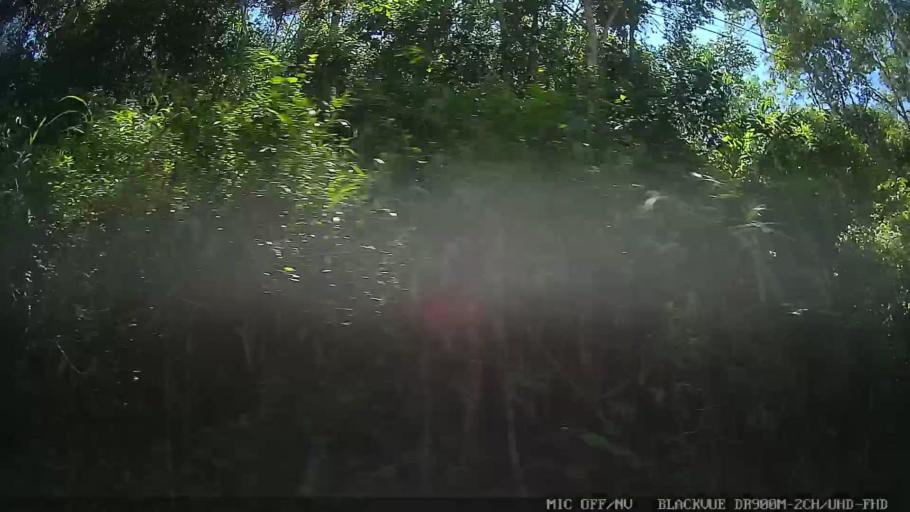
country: BR
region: Sao Paulo
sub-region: Mogi das Cruzes
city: Mogi das Cruzes
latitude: -23.5826
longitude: -46.1477
